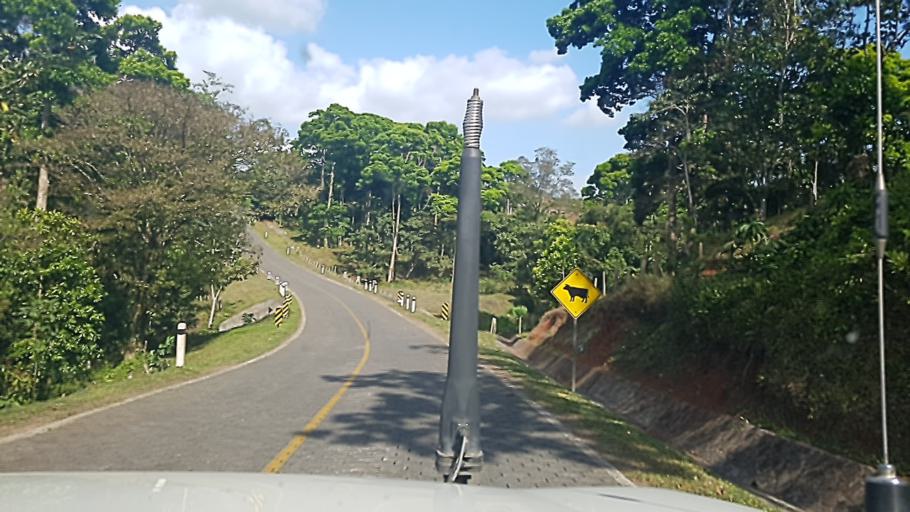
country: NI
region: Atlantico Sur
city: Nueva Guinea
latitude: 11.6977
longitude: -84.3940
